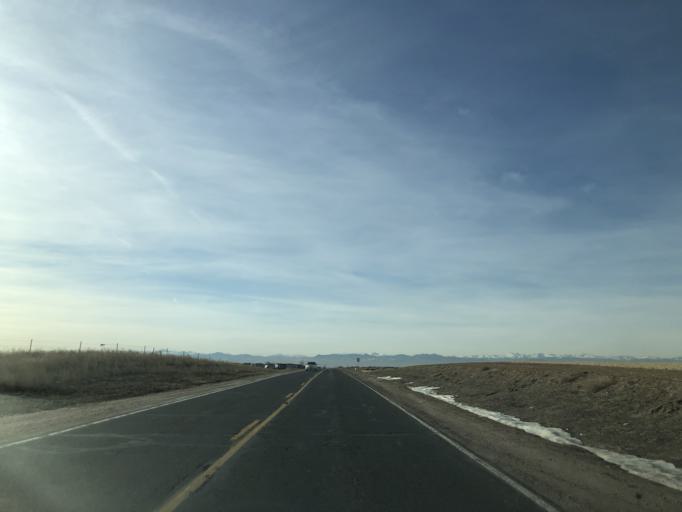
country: US
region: Colorado
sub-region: Adams County
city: Aurora
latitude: 39.7983
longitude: -104.7265
